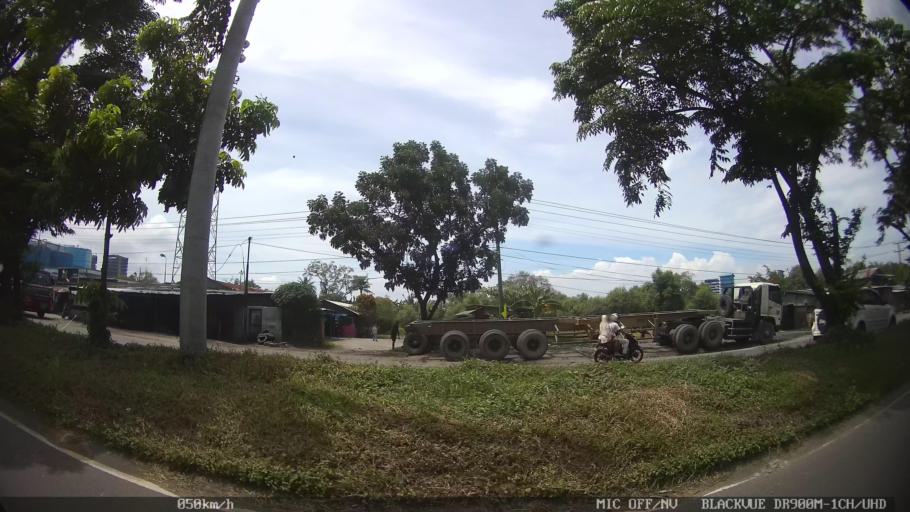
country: ID
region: North Sumatra
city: Belawan
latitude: 3.7811
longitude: 98.6908
